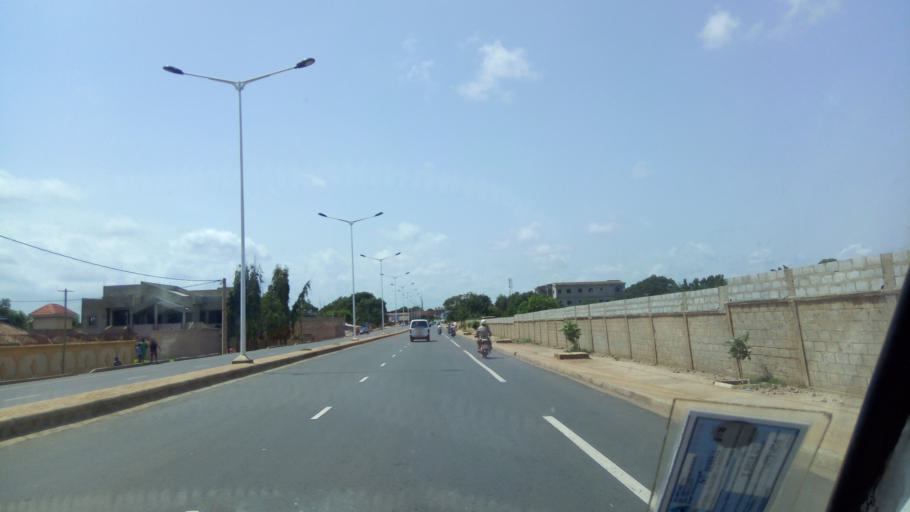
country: TG
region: Maritime
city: Lome
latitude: 6.1846
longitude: 1.2560
